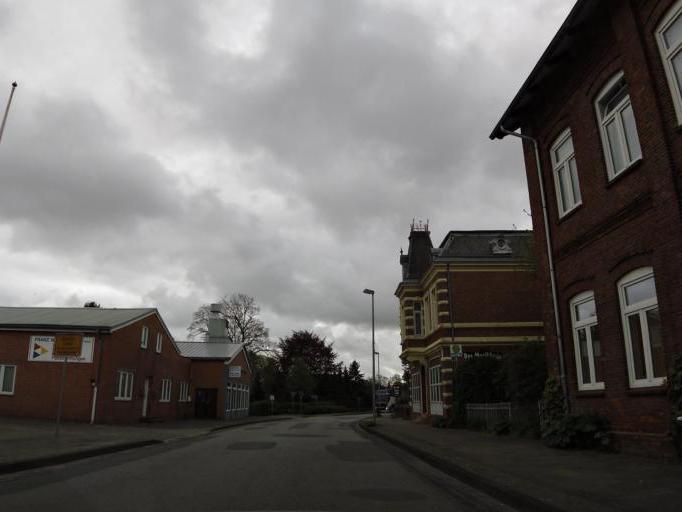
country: DE
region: Schleswig-Holstein
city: Niebull
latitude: 54.7817
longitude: 8.8220
